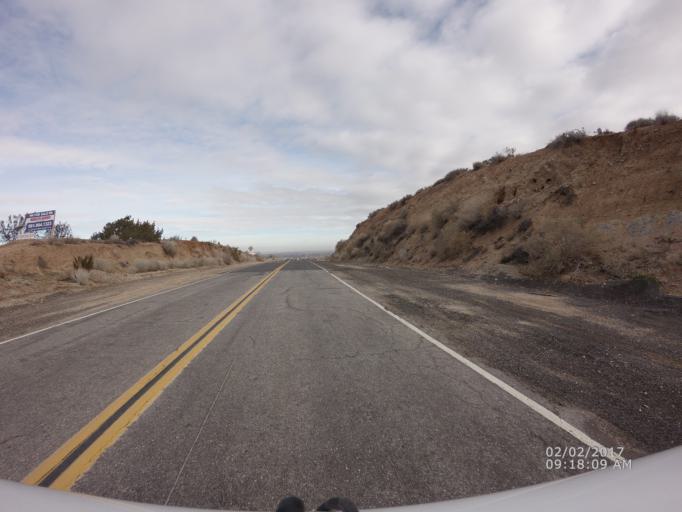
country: US
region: California
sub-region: Los Angeles County
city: Vincent
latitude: 34.5286
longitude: -118.0584
